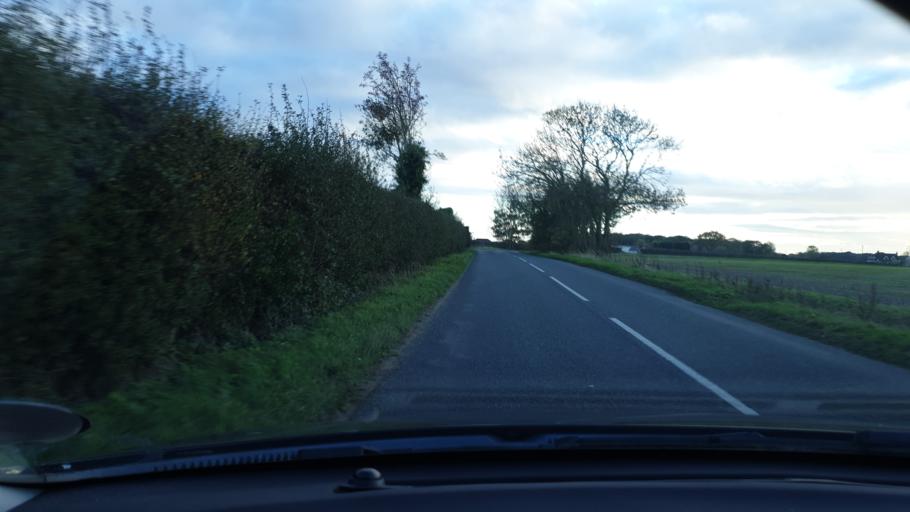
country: GB
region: England
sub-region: Essex
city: Mistley
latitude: 51.9026
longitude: 1.1433
